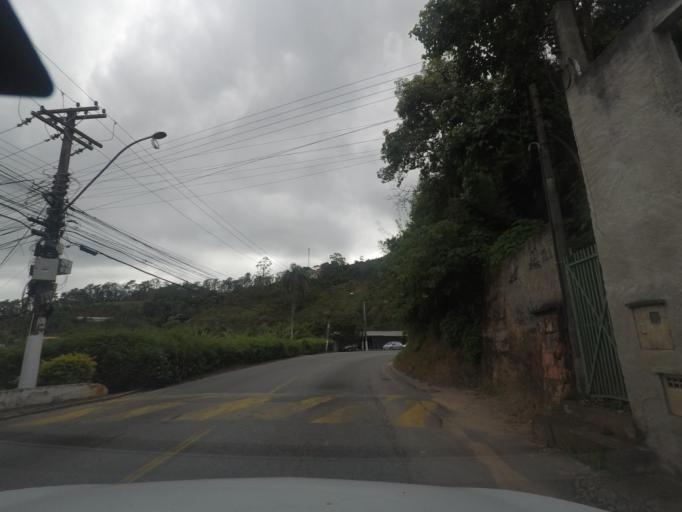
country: BR
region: Rio de Janeiro
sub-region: Teresopolis
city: Teresopolis
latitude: -22.3872
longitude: -42.9555
